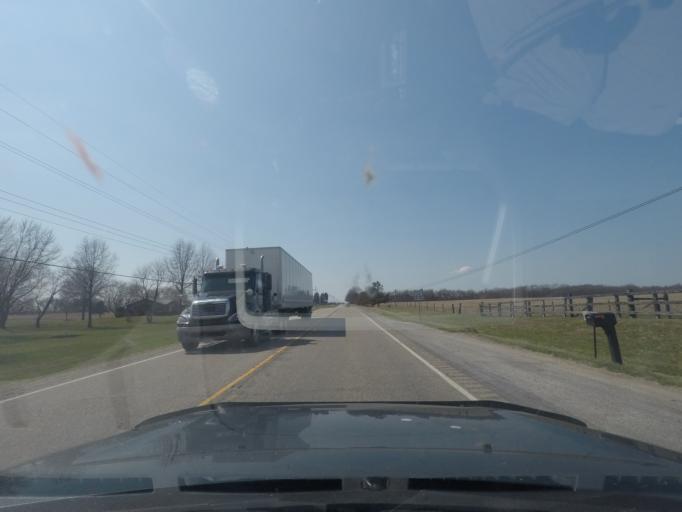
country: US
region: Indiana
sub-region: LaPorte County
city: LaPorte
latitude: 41.5915
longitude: -86.7815
